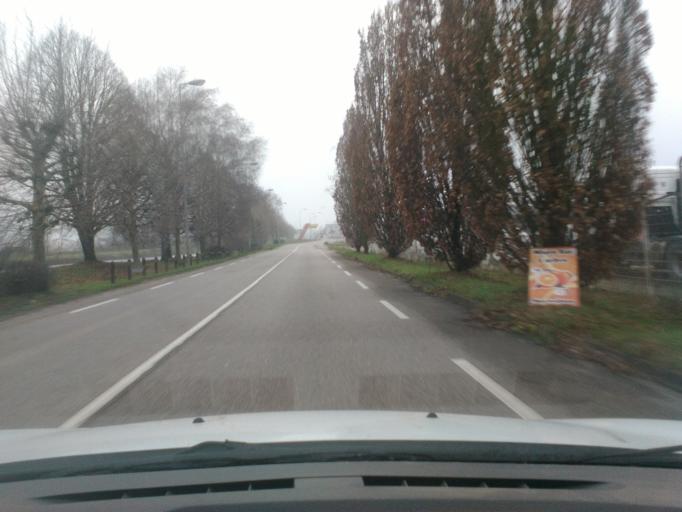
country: FR
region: Lorraine
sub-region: Departement des Vosges
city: Chavelot
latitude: 48.2184
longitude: 6.4376
